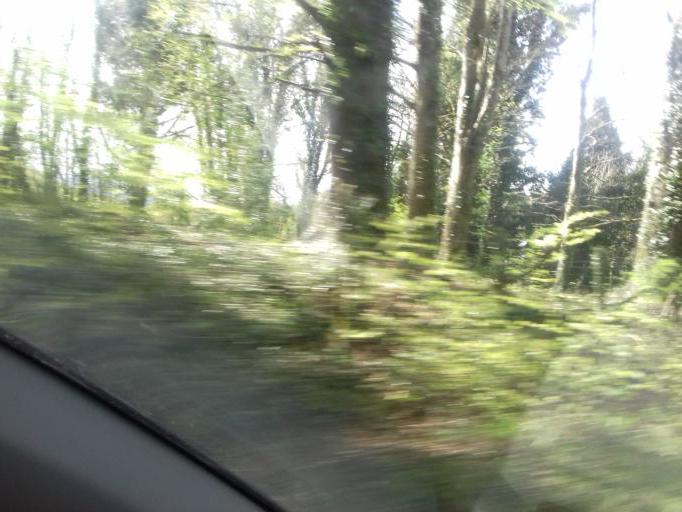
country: GB
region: Northern Ireland
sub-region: Fermanagh District
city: Enniskillen
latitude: 54.3934
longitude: -7.7028
